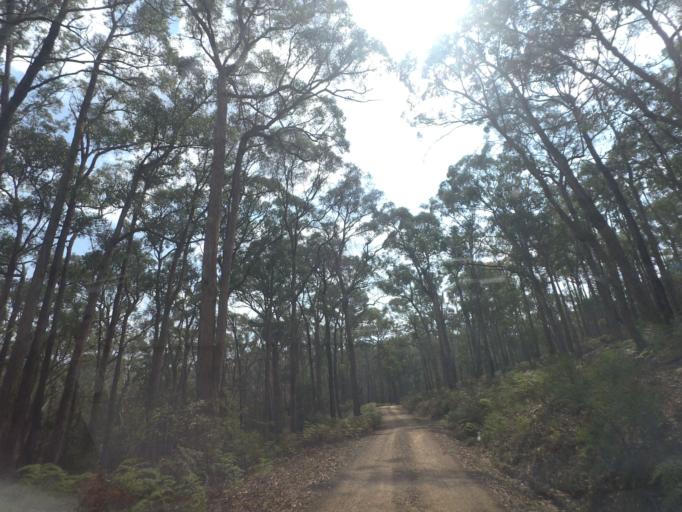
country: AU
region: Victoria
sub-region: Moorabool
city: Bacchus Marsh
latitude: -37.4645
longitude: 144.3684
